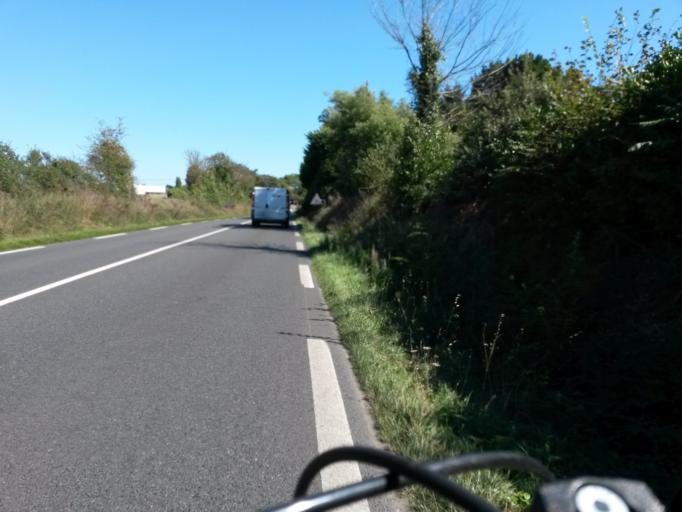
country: FR
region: Pays de la Loire
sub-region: Departement de la Loire-Atlantique
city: Guerande
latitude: 47.3292
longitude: -2.4492
